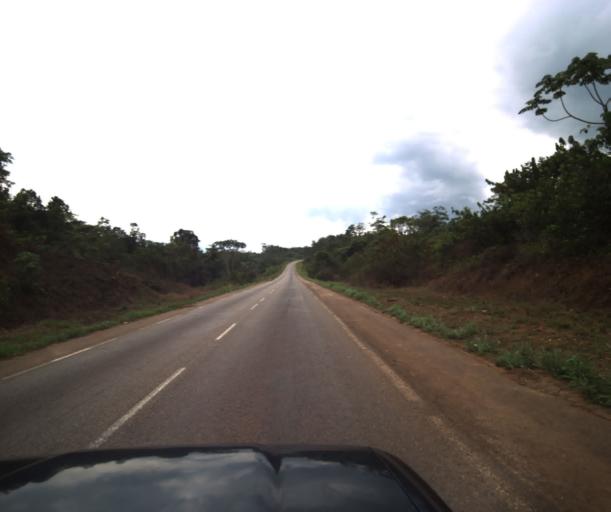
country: CM
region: Littoral
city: Edea
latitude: 3.8718
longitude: 10.0723
